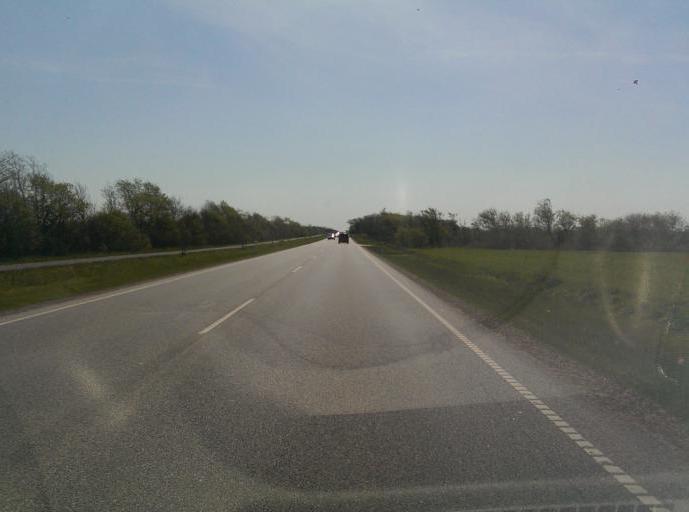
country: DK
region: South Denmark
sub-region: Esbjerg Kommune
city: Ribe
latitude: 55.3747
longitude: 8.7615
